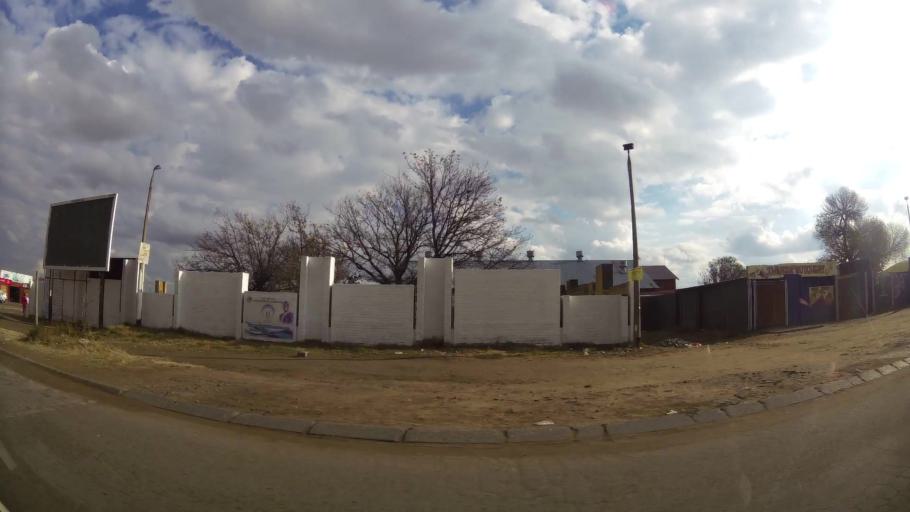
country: ZA
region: Orange Free State
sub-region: Fezile Dabi District Municipality
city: Sasolburg
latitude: -26.8367
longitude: 27.8431
